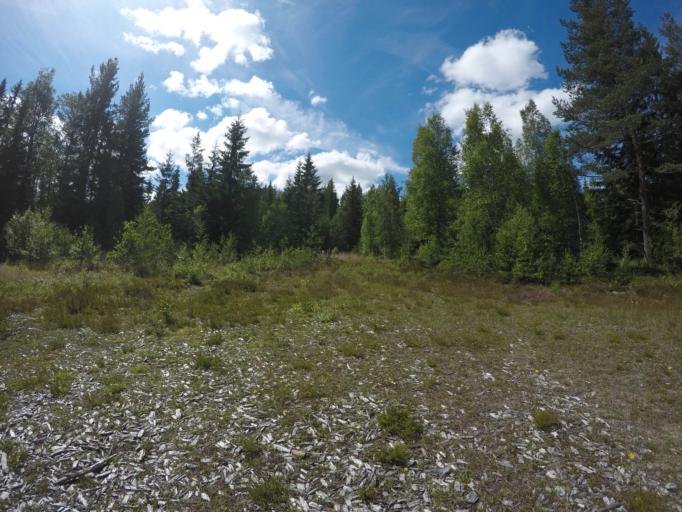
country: SE
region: OErebro
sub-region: Hallefors Kommun
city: Haellefors
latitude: 60.0924
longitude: 14.4761
